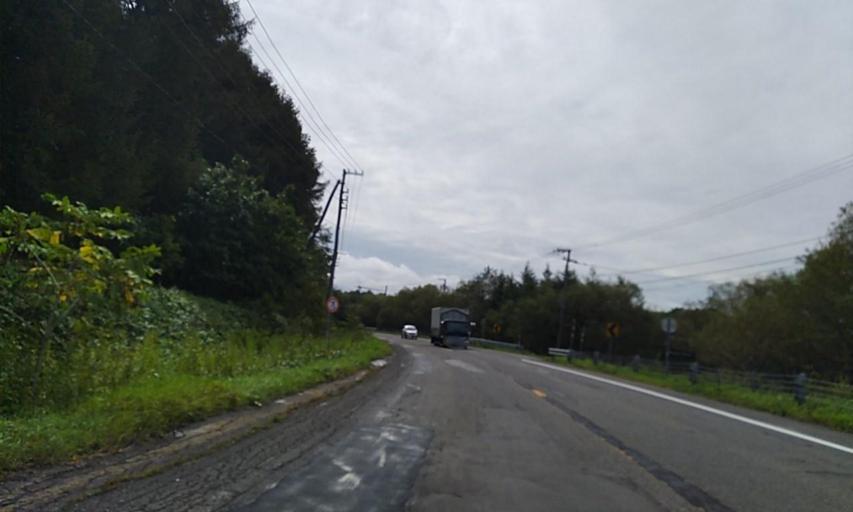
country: JP
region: Hokkaido
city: Shibetsu
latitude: 43.6155
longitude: 145.1792
